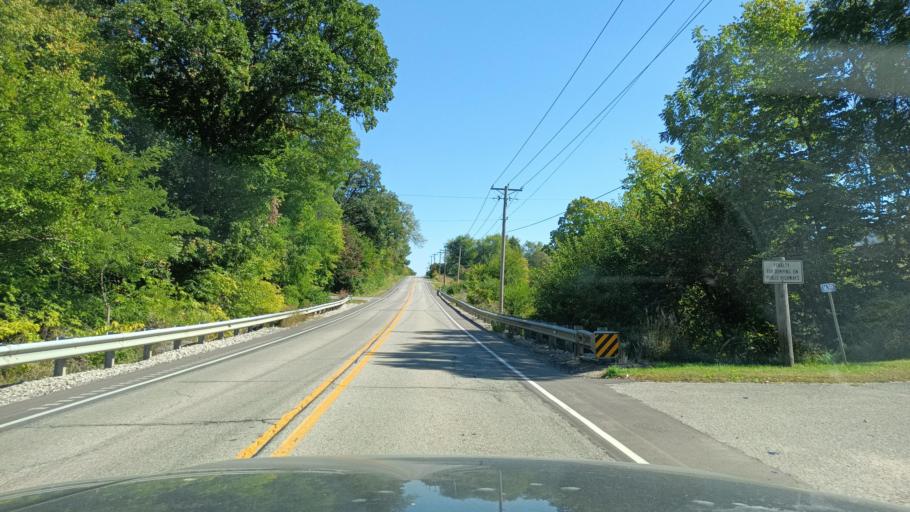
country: US
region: Illinois
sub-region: McLean County
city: Danvers
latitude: 40.6169
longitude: -89.2248
